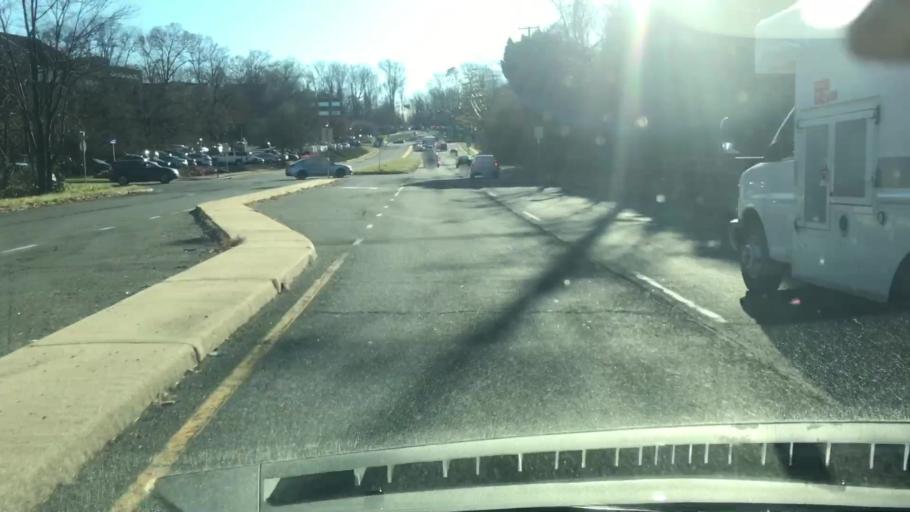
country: US
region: Virginia
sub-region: Fairfax County
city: Merrifield
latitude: 38.8682
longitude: -77.2389
